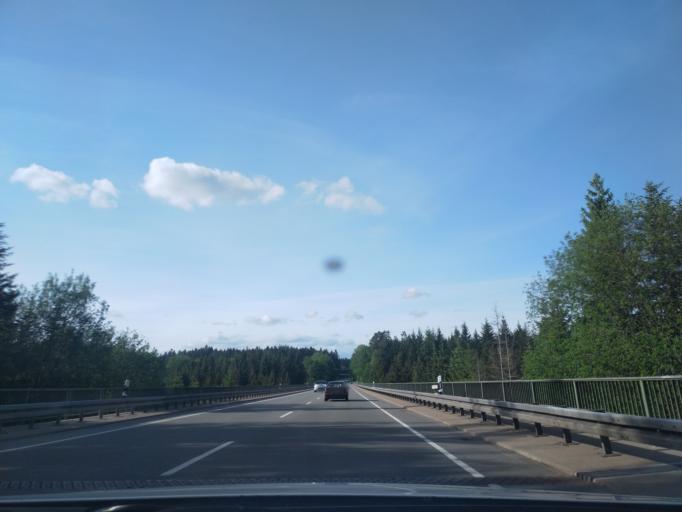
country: DE
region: Baden-Wuerttemberg
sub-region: Karlsruhe Region
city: Freudenstadt
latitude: 48.4412
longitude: 8.4404
